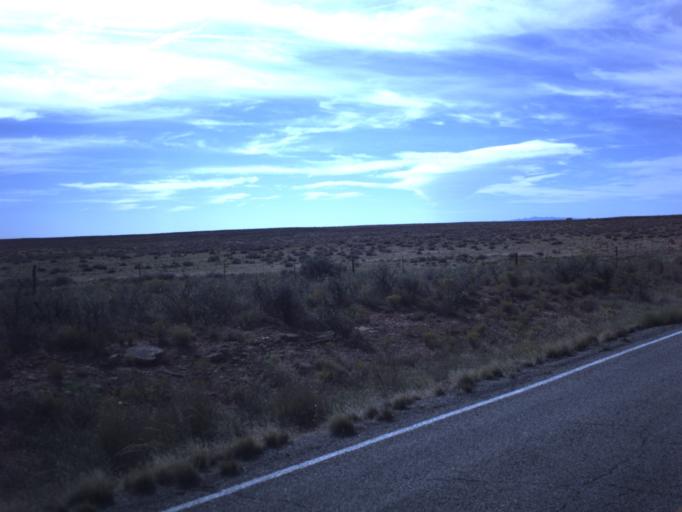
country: US
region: Utah
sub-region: San Juan County
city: Blanding
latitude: 37.3462
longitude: -109.3482
